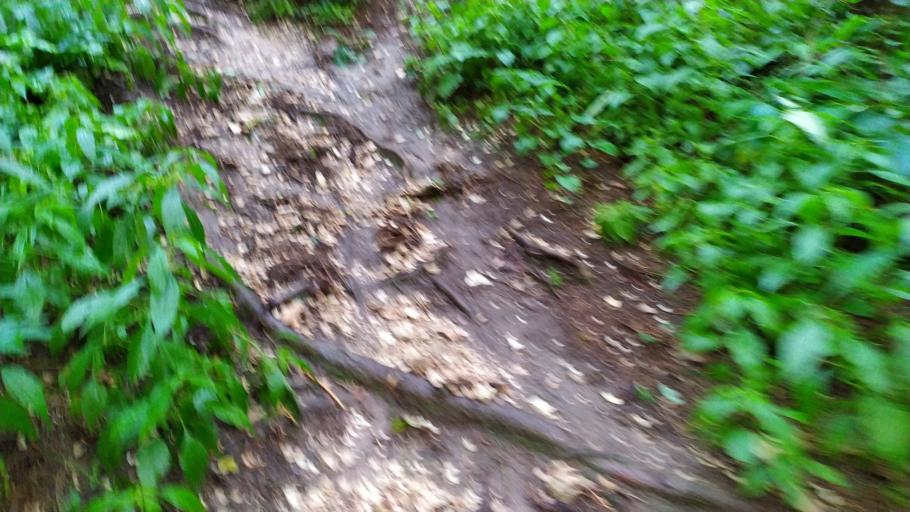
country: IT
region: Veneto
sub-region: Provincia di Vicenza
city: Torrebelvicino
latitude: 45.6939
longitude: 11.3262
